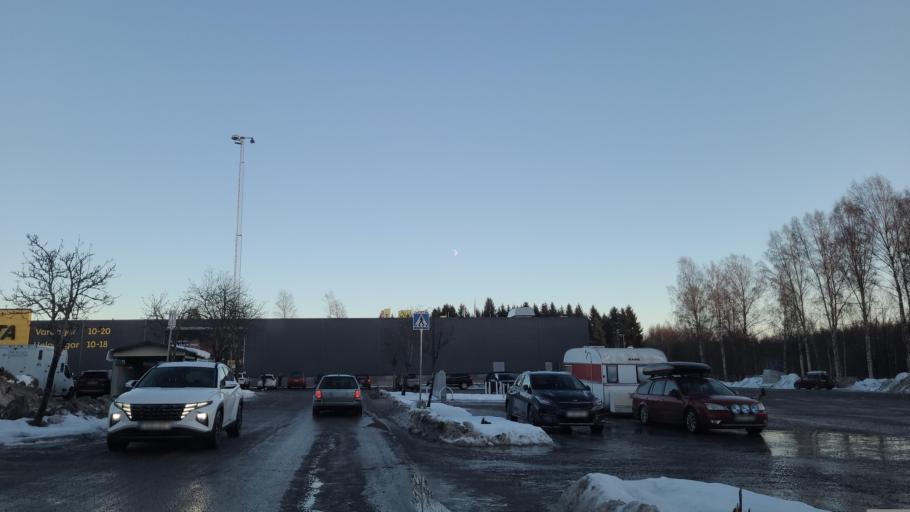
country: SE
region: Gaevleborg
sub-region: Soderhamns Kommun
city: Soderhamn
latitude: 61.2944
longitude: 17.0197
